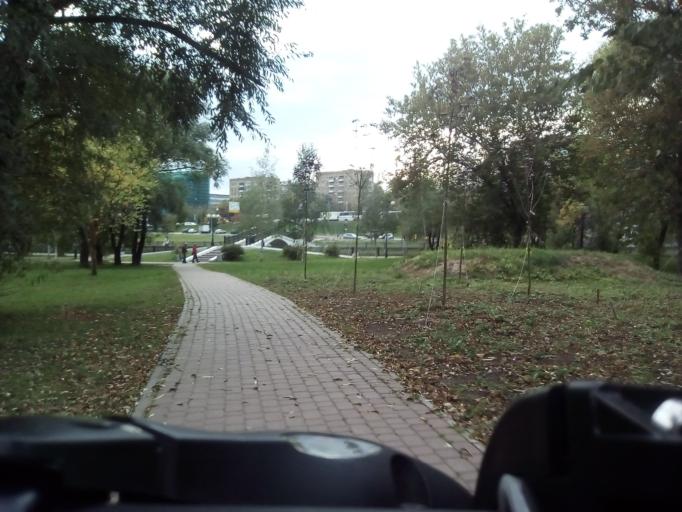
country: RU
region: Moscow
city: Rostokino
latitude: 55.8324
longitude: 37.6564
